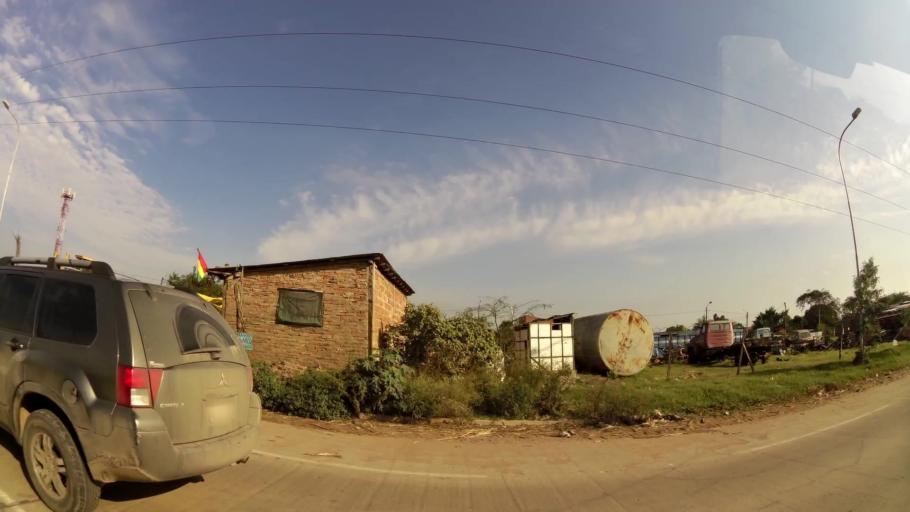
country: BO
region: Santa Cruz
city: Santa Cruz de la Sierra
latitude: -17.7234
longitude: -63.1331
